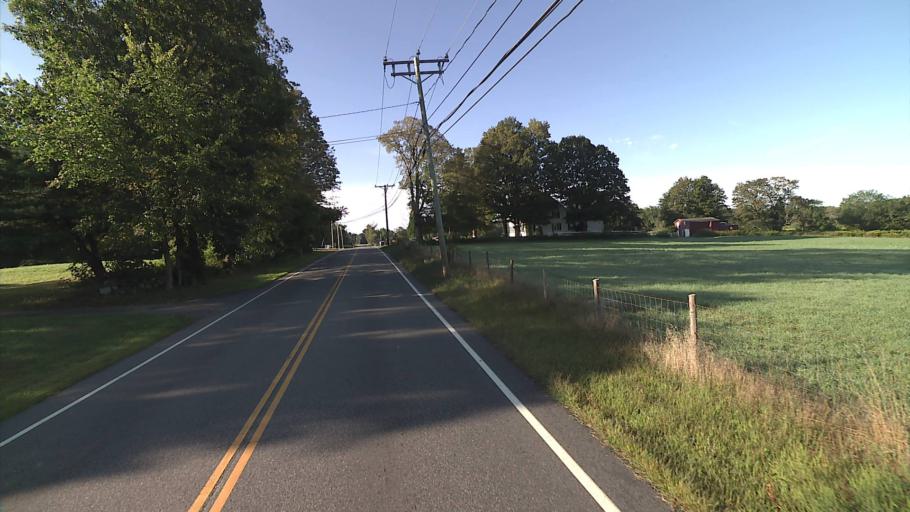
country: US
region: Connecticut
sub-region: Windham County
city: South Windham
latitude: 41.6453
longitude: -72.1611
